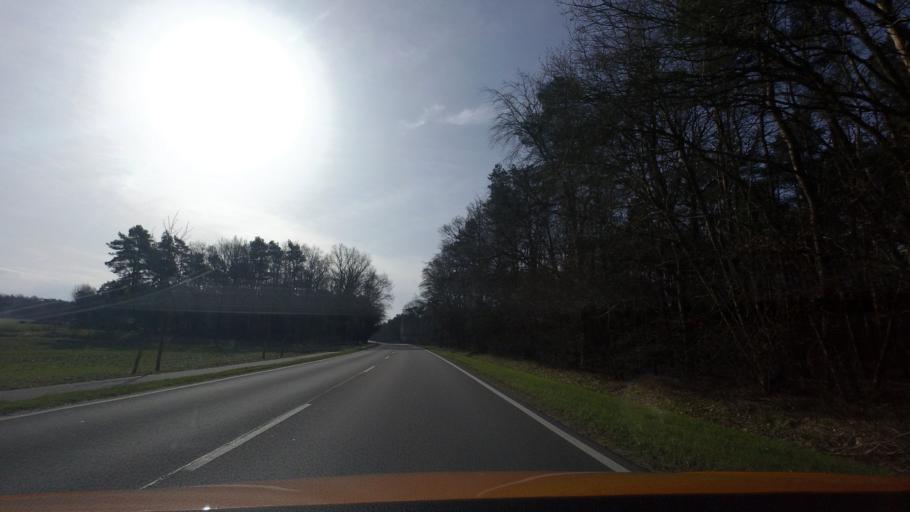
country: DE
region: Lower Saxony
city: Kirchdorf
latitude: 52.5838
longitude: 8.8386
